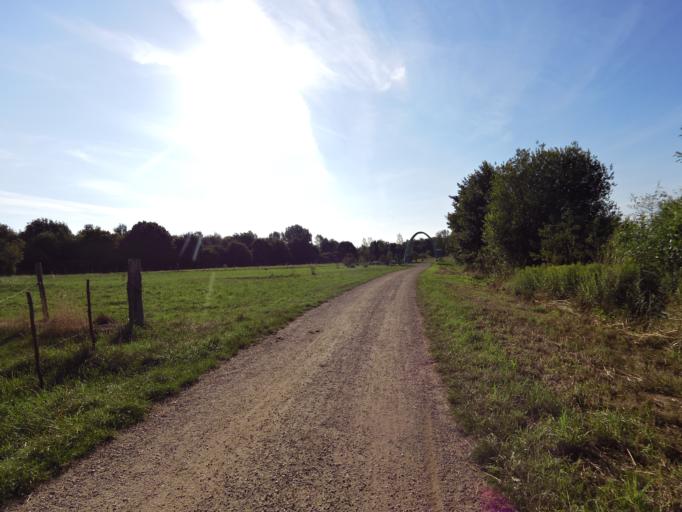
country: DE
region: North Rhine-Westphalia
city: Huckelhoven
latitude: 51.0510
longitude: 6.2038
